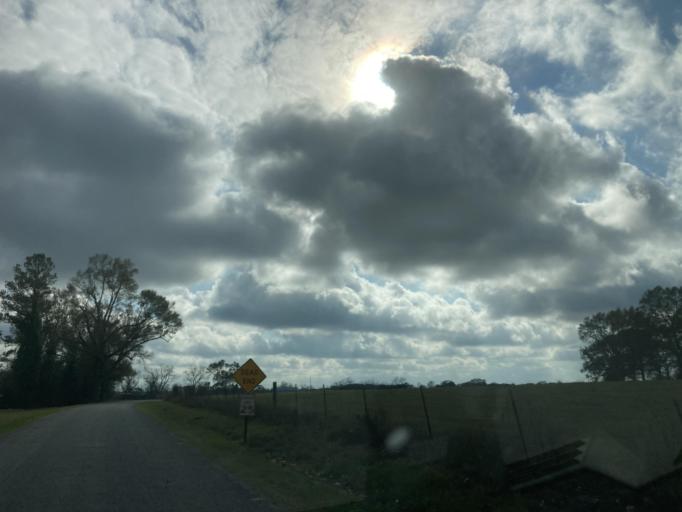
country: US
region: Mississippi
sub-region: Stone County
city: Wiggins
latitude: 30.8107
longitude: -89.1002
